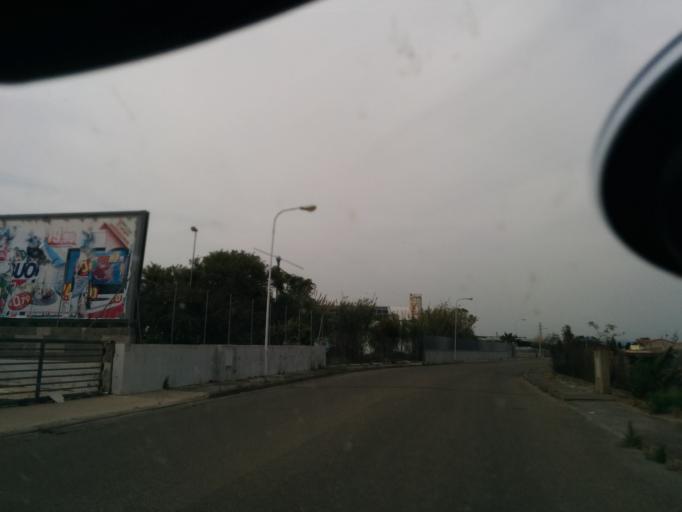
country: IT
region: Sardinia
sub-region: Provincia di Carbonia-Iglesias
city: Sant'Antioco
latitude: 39.0489
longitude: 8.4570
